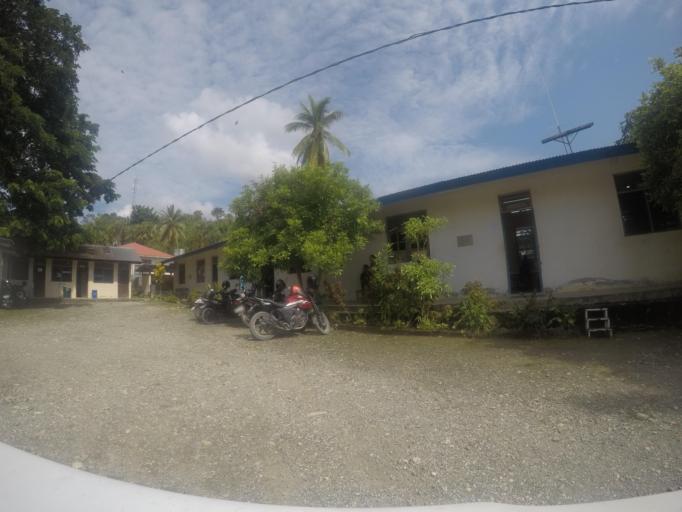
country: TL
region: Viqueque
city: Viqueque
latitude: -8.8524
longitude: 126.3581
